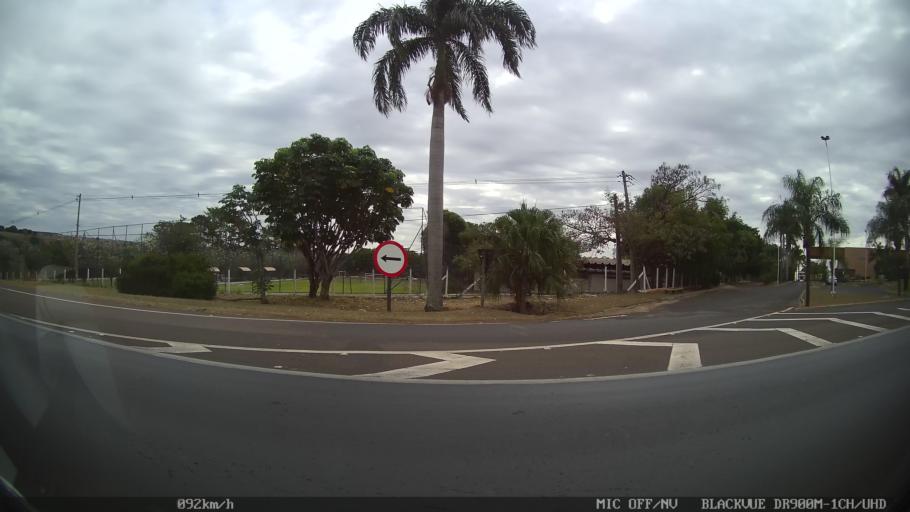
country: BR
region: Sao Paulo
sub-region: Sao Jose Do Rio Preto
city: Sao Jose do Rio Preto
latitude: -20.8161
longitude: -49.4443
